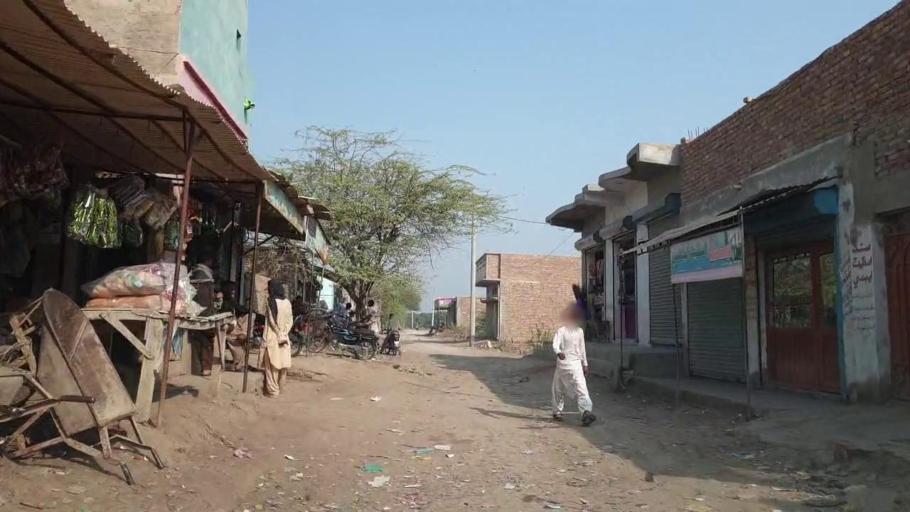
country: PK
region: Sindh
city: Mirpur Khas
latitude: 25.5452
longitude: 69.0214
